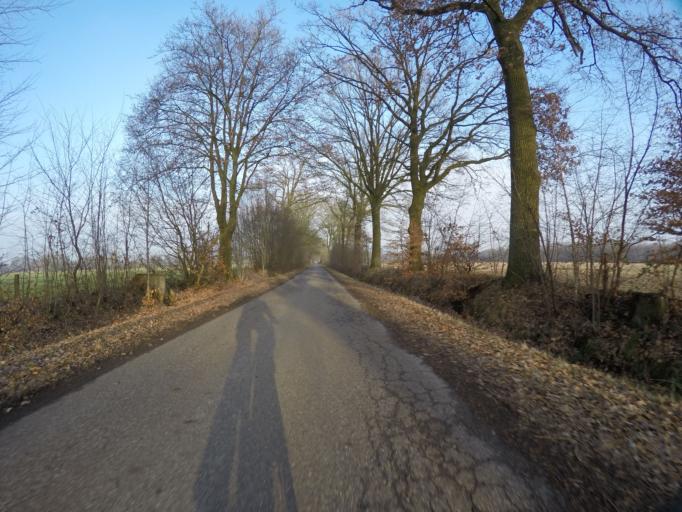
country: DE
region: Schleswig-Holstein
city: Hasloh
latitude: 53.7064
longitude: 9.8860
